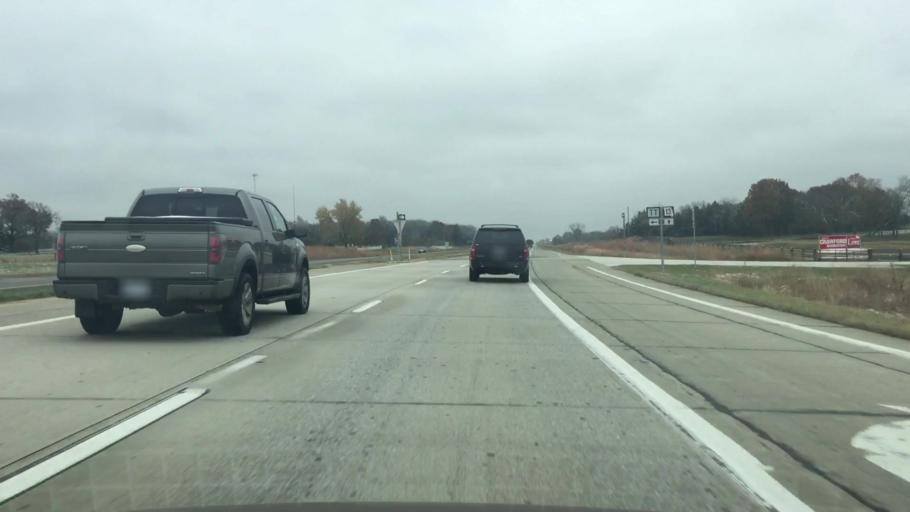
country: US
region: Missouri
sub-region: Saint Clair County
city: Osceola
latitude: 38.0104
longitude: -93.6581
